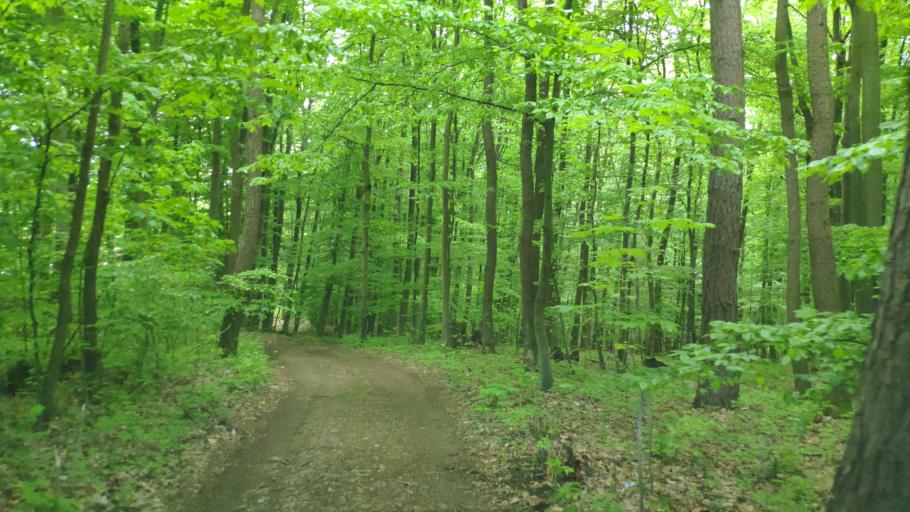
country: SK
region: Kosicky
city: Kosice
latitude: 48.7584
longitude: 21.1978
